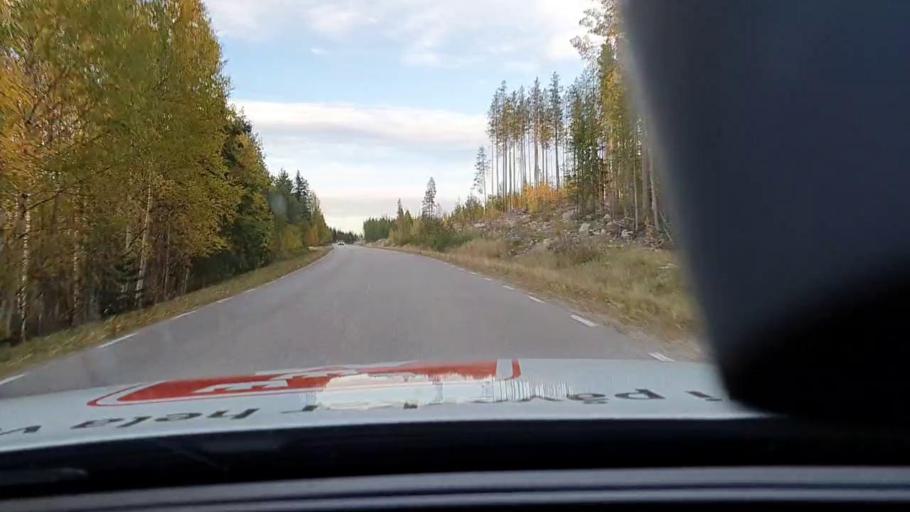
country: SE
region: Norrbotten
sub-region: Overkalix Kommun
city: OEverkalix
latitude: 66.3253
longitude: 22.7684
